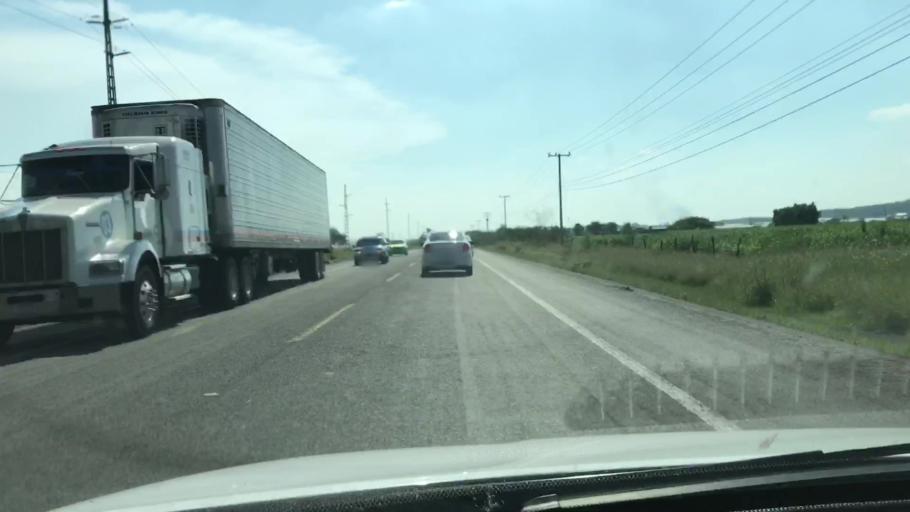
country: MX
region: Michoacan
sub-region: Vista Hermosa
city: Los Pilares
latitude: 20.2761
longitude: -102.3911
